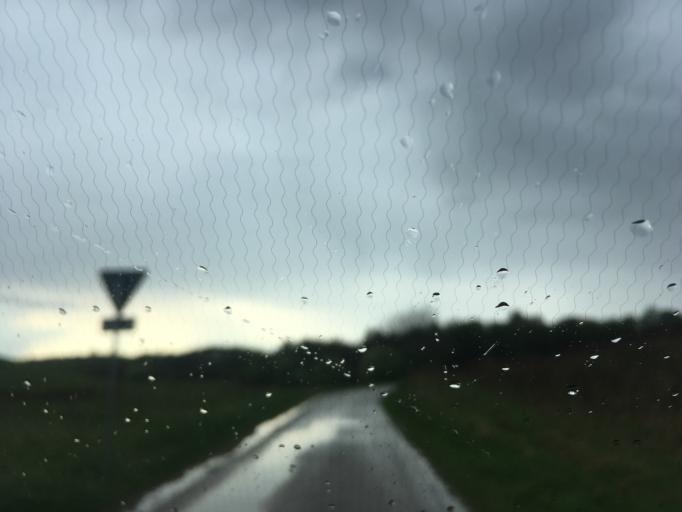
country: PL
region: Warmian-Masurian Voivodeship
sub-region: Powiat dzialdowski
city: Rybno
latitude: 53.3769
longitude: 19.9954
